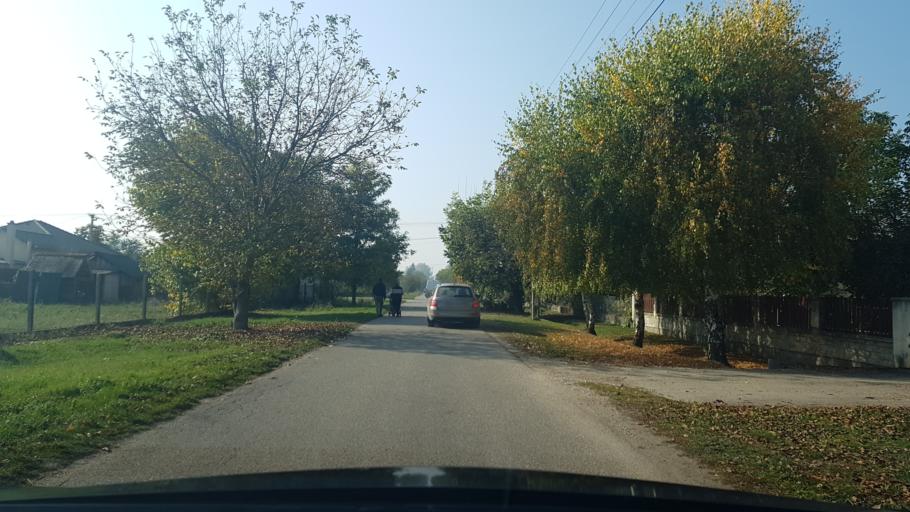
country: HU
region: Fejer
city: Pusztaszabolcs
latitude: 47.1450
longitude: 18.7584
